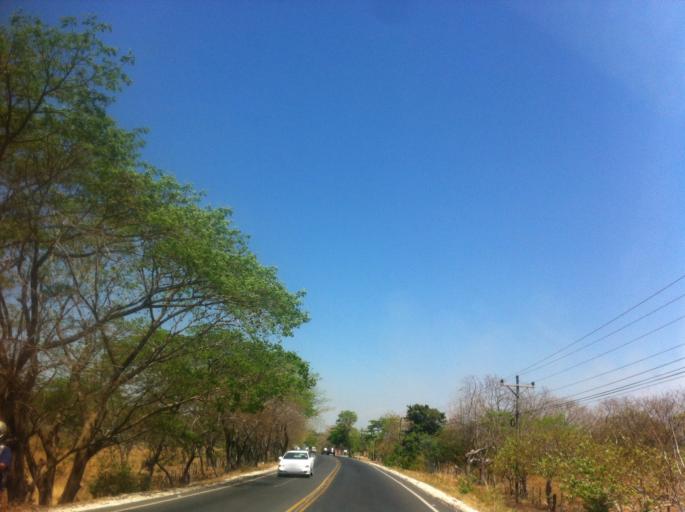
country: CR
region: Guanacaste
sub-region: Canton de Nicoya
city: Nicoya
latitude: 10.1893
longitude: -85.4718
